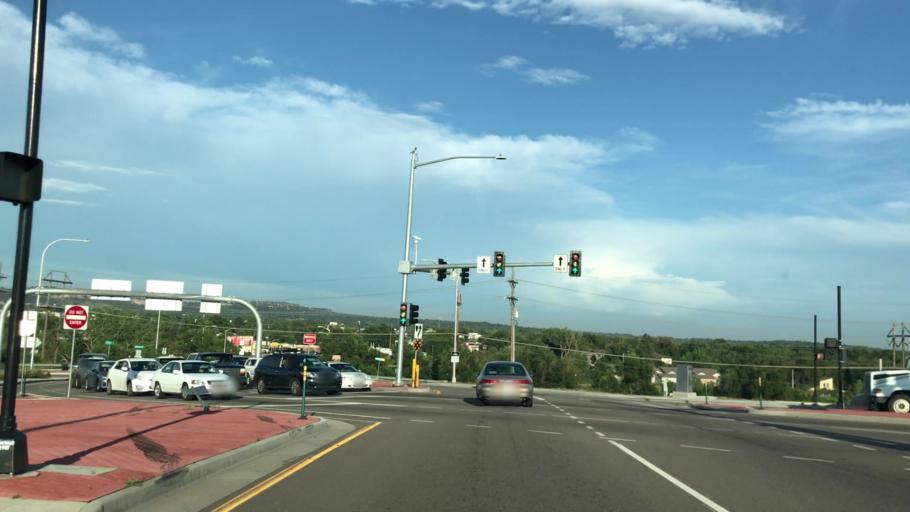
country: US
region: Colorado
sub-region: El Paso County
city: Colorado Springs
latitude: 38.8764
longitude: -104.8342
